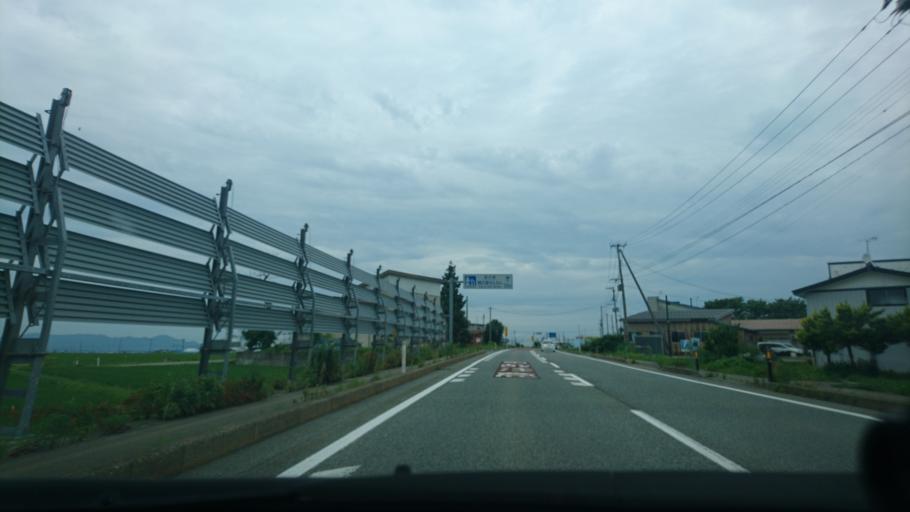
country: JP
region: Akita
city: Yokotemachi
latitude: 39.3749
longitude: 140.5691
